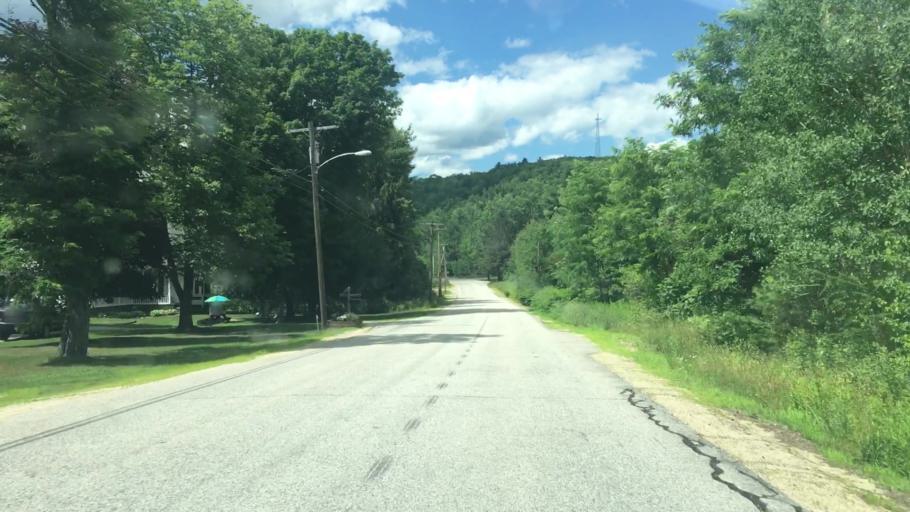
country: US
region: Maine
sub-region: Franklin County
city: Jay
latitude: 44.5332
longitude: -70.2260
